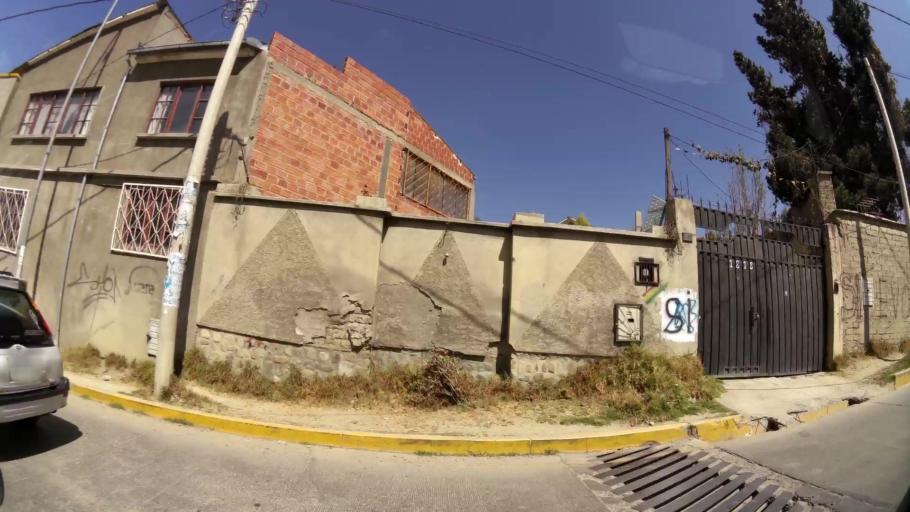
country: BO
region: La Paz
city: La Paz
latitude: -16.5355
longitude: -68.1370
